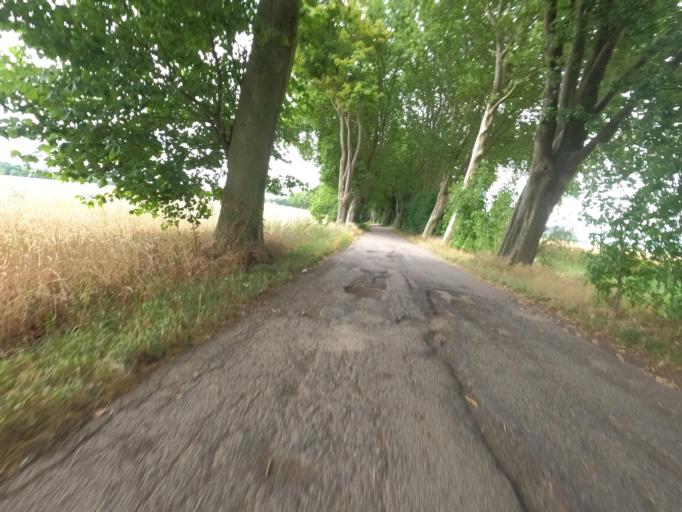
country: DE
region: North Rhine-Westphalia
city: Siersdorf
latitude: 50.9030
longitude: 6.2411
